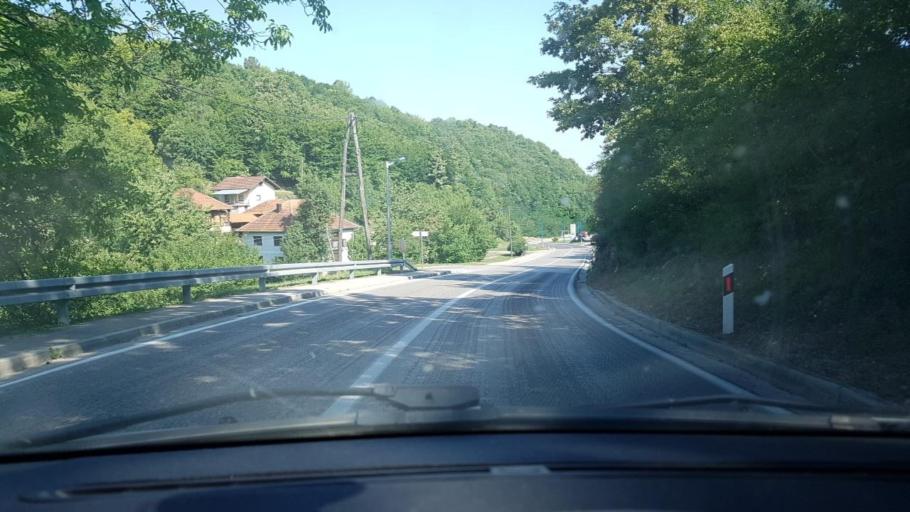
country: BA
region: Federation of Bosnia and Herzegovina
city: Pecigrad
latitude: 45.0563
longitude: 15.8939
